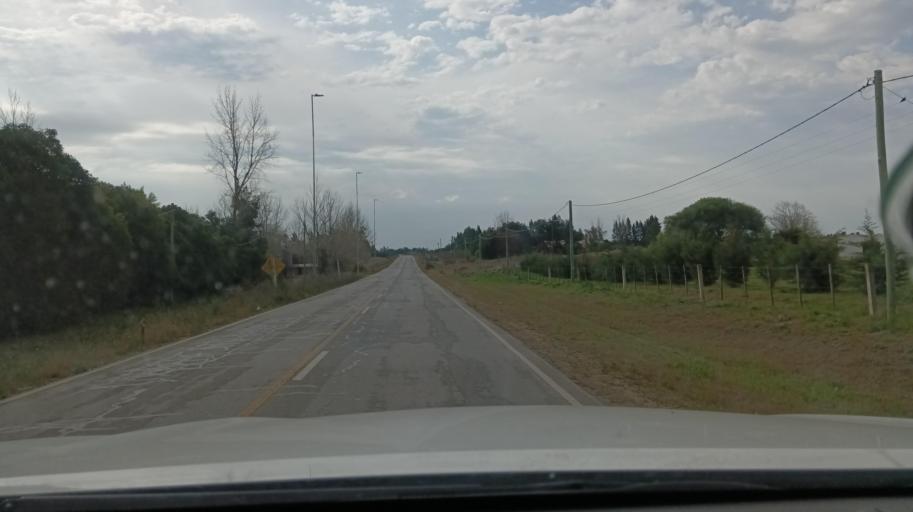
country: UY
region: Canelones
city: Sauce
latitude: -34.6615
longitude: -56.1094
